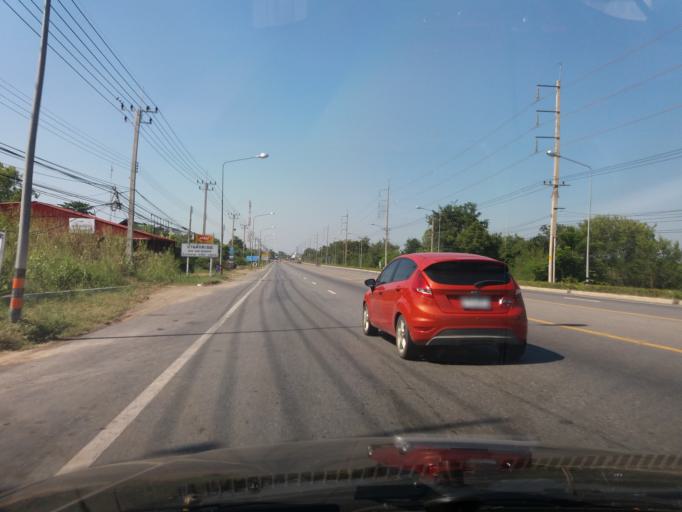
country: TH
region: Chai Nat
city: Wat Sing
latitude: 15.2553
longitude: 100.0957
